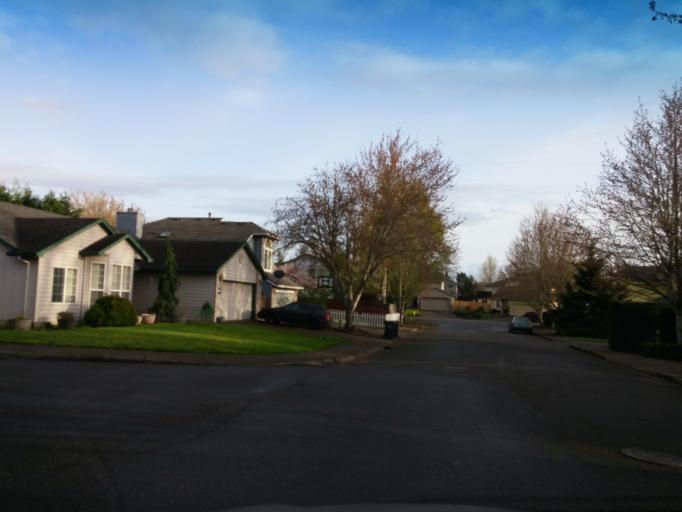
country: US
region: Oregon
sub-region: Washington County
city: Aloha
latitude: 45.5173
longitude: -122.8567
